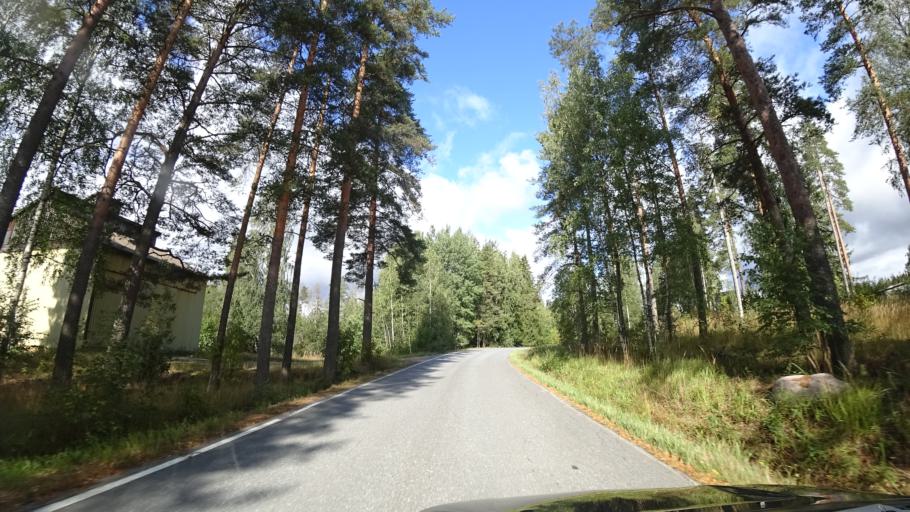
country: FI
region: Haeme
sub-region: Riihimaeki
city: Oitti
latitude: 60.6885
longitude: 24.9990
